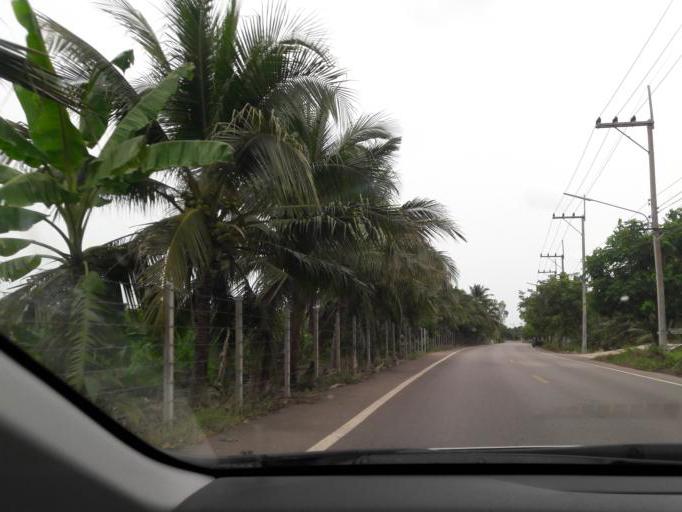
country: TH
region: Samut Sakhon
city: Ban Phaeo
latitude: 13.5675
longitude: 100.0431
